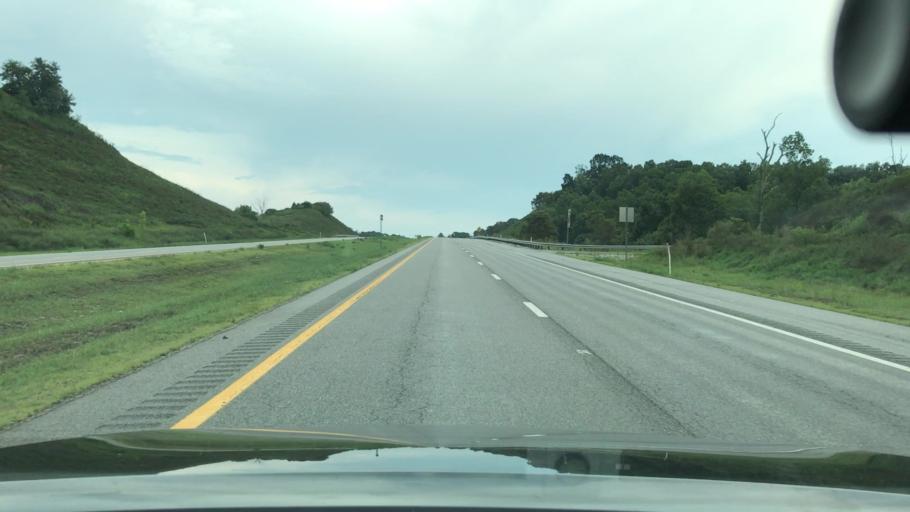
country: US
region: West Virginia
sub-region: Mason County
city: Point Pleasant
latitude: 38.7963
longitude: -82.0976
